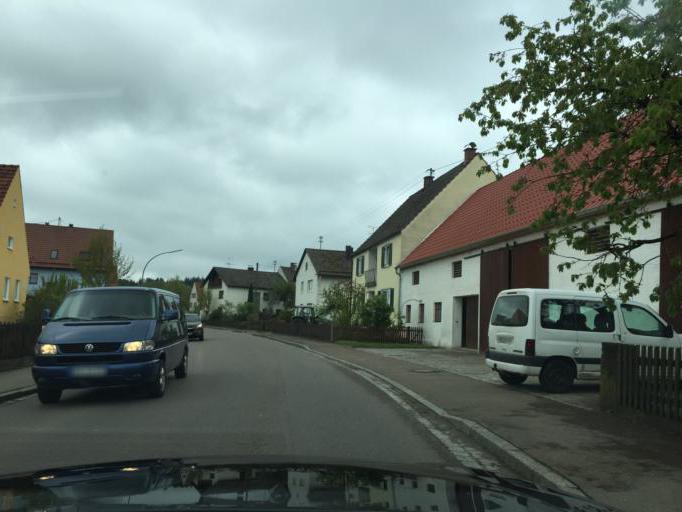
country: DE
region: Bavaria
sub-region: Swabia
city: Buttenwiesen
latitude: 48.5818
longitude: 10.7141
